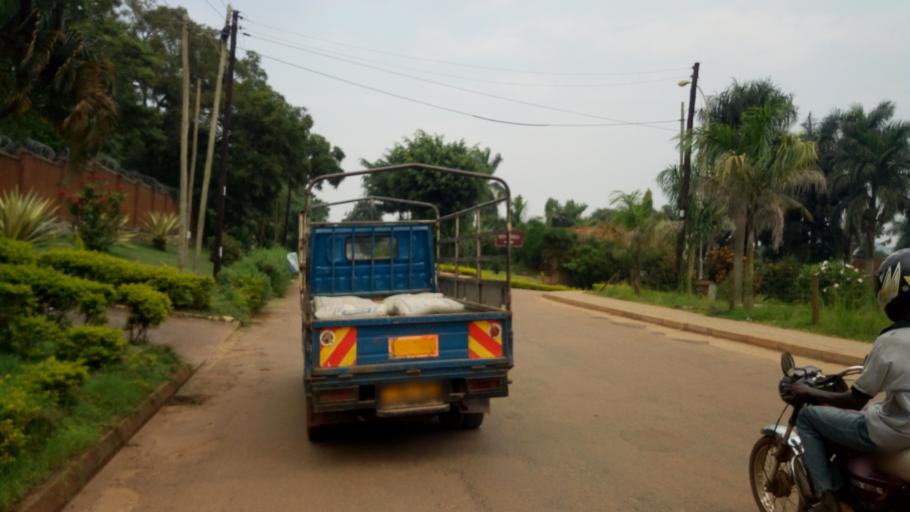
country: UG
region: Central Region
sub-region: Kampala District
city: Kampala
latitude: 0.3104
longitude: 32.6194
